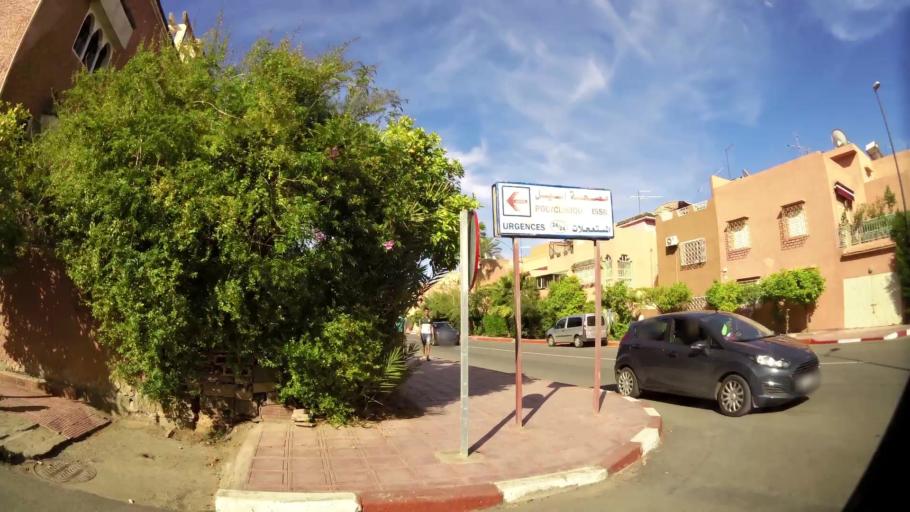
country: MA
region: Marrakech-Tensift-Al Haouz
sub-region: Marrakech
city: Marrakesh
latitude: 31.6587
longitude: -8.0099
